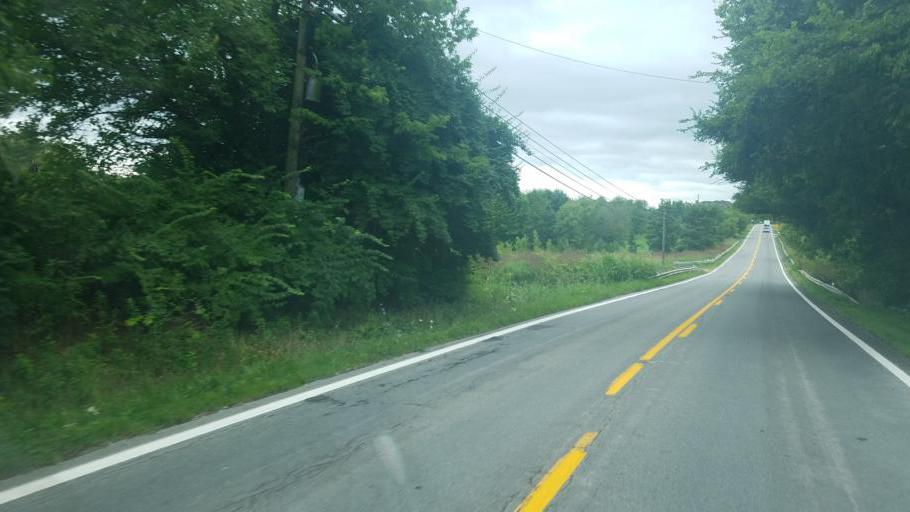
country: US
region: Ohio
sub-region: Franklin County
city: Grove City
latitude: 39.8718
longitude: -83.0274
